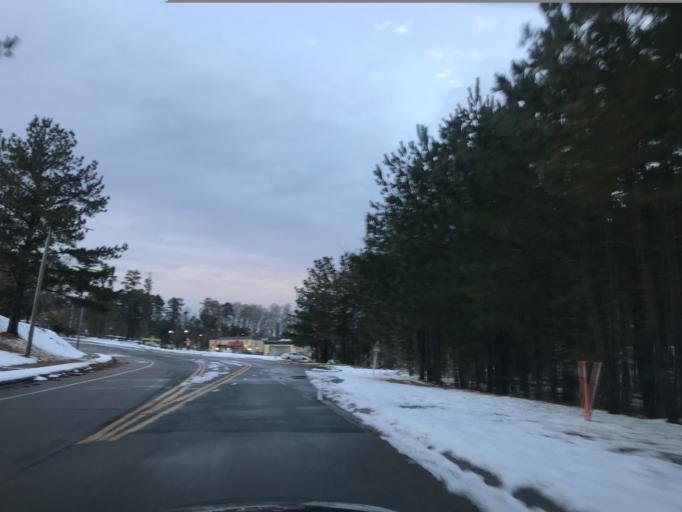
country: US
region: North Carolina
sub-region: Wake County
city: Rolesville
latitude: 35.8741
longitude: -78.5388
